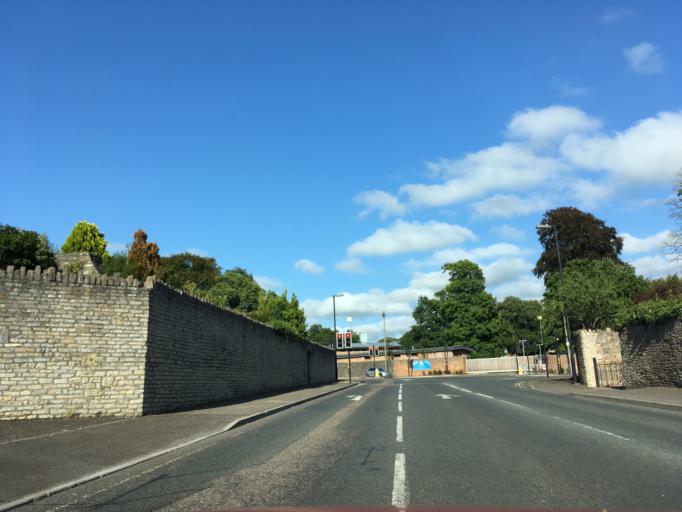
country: GB
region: England
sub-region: Somerset
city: Wells
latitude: 51.2126
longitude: -2.6475
